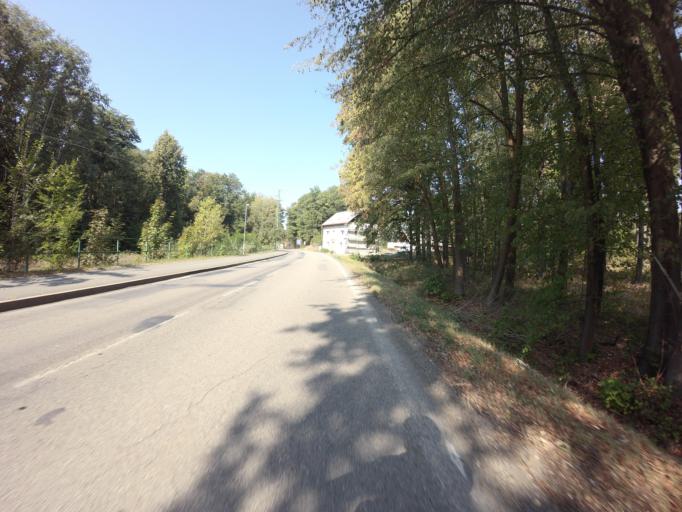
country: CZ
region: Central Bohemia
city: Tynec nad Sazavou
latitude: 49.8279
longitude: 14.6023
